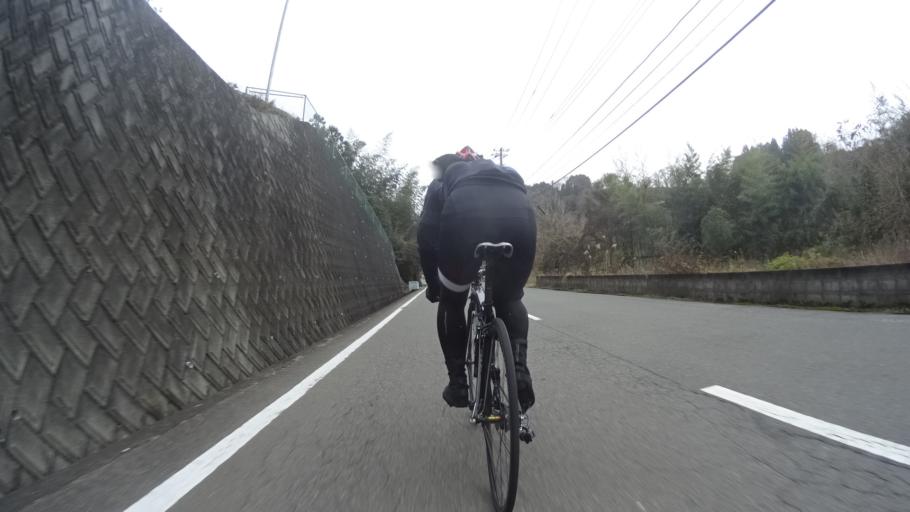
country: JP
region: Yamanashi
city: Uenohara
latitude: 35.6379
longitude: 139.0860
